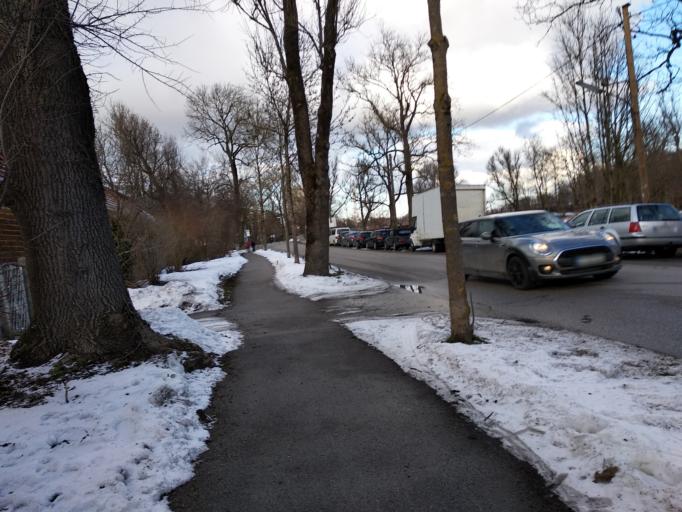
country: DE
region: Bavaria
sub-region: Upper Bavaria
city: Munich
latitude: 48.0997
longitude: 11.5480
